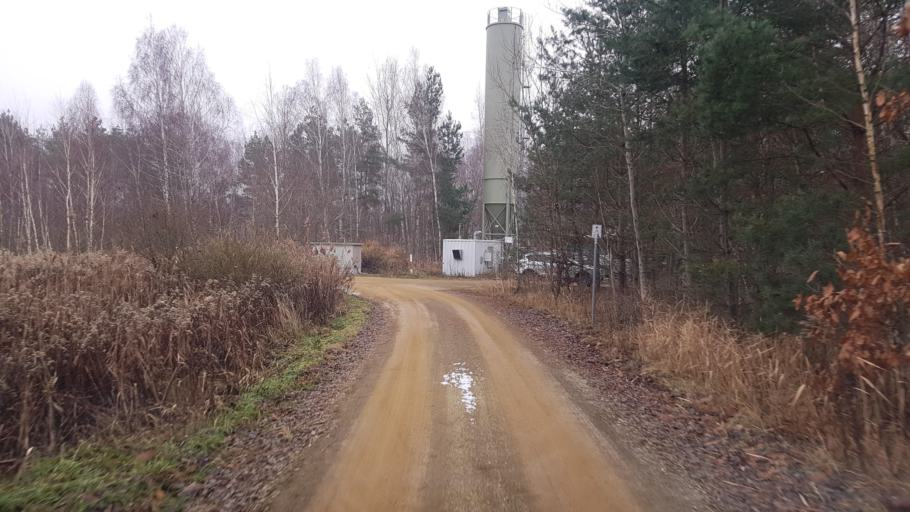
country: DE
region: Brandenburg
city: Plessa
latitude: 51.4953
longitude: 13.6585
